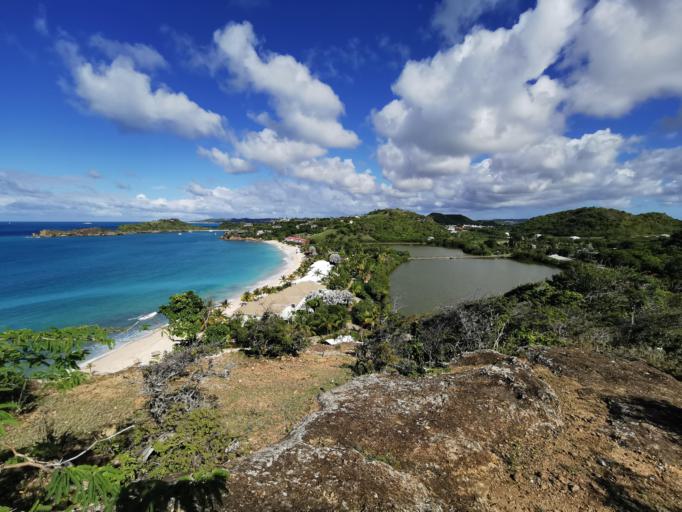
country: AG
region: Saint John
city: Saint John's
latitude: 17.1197
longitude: -61.8964
